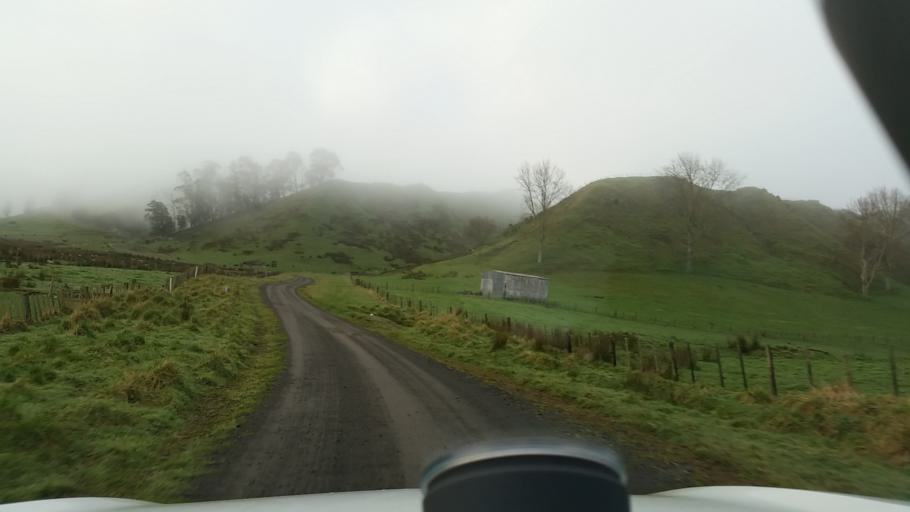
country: NZ
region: Taranaki
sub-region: South Taranaki District
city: Eltham
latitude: -39.4302
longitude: 174.4405
